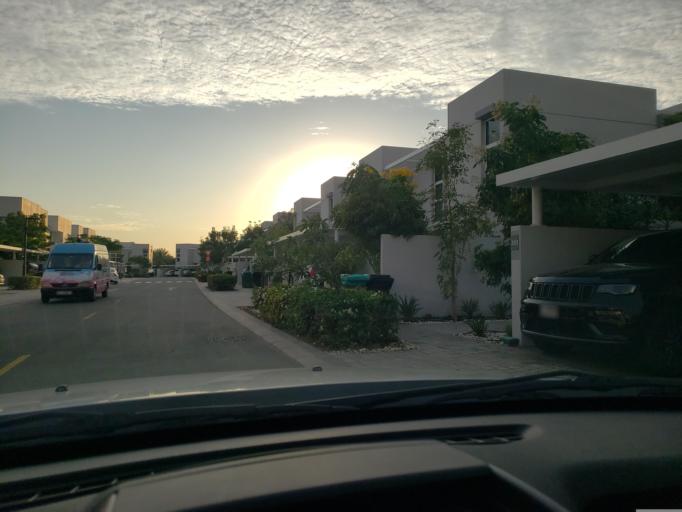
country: AE
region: Dubai
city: Dubai
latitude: 25.0137
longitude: 55.2690
